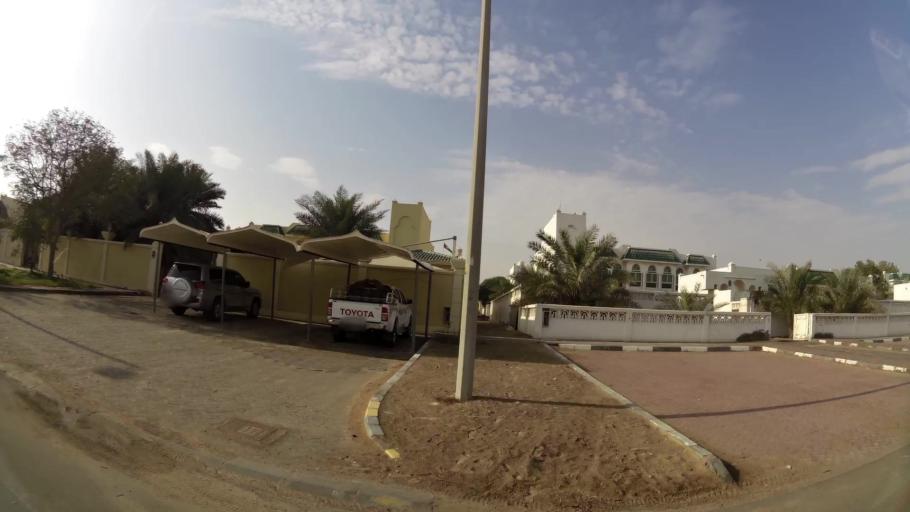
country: AE
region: Abu Dhabi
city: Abu Dhabi
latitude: 24.2632
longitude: 54.6709
